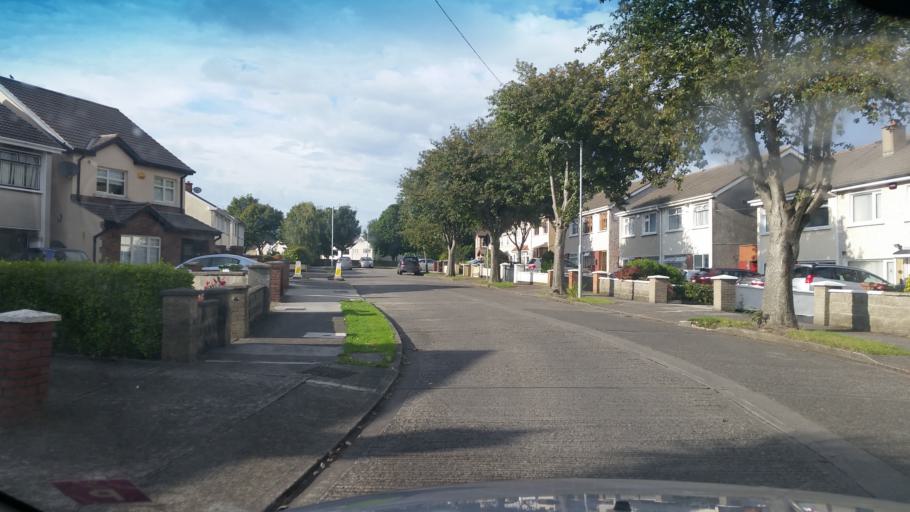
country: IE
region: Leinster
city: Donaghmede
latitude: 53.3934
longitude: -6.1651
